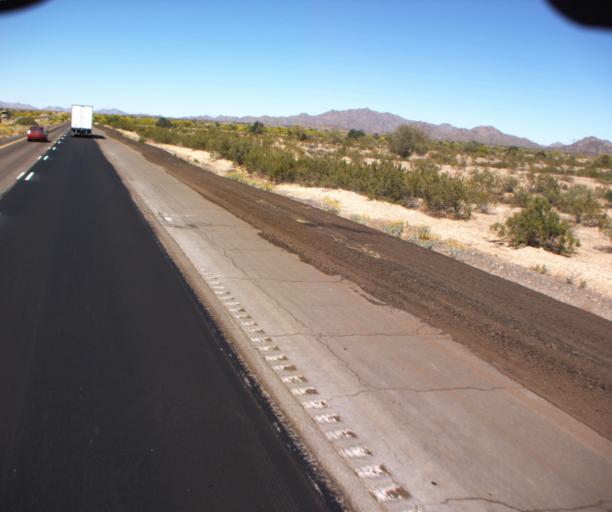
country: US
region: Arizona
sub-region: Maricopa County
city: Gila Bend
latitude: 33.0679
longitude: -112.6454
